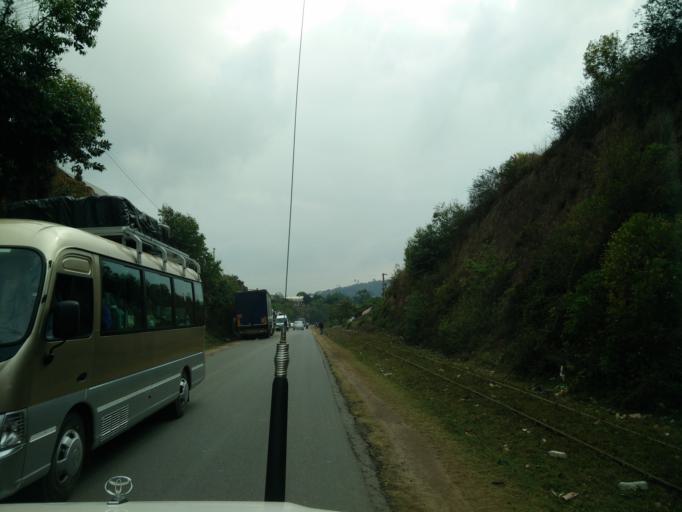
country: MG
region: Upper Matsiatra
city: Fianarantsoa
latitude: -21.4323
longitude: 47.1202
